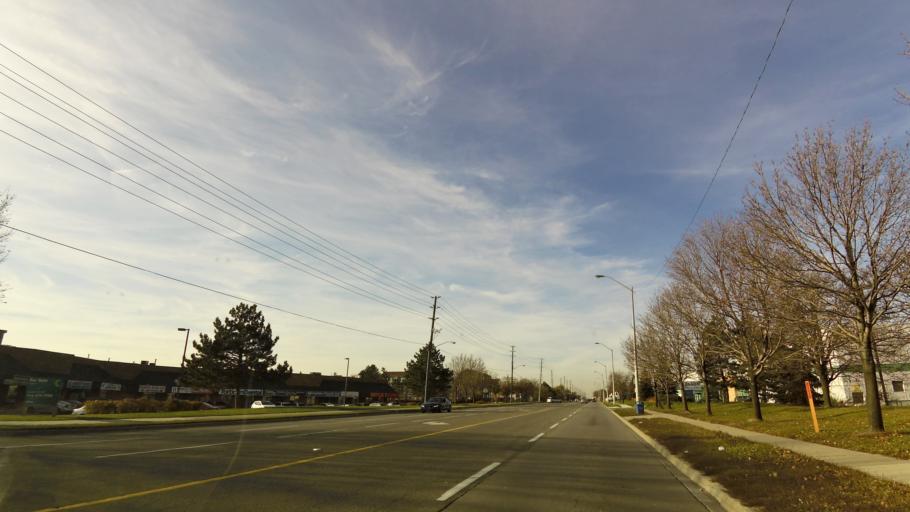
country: CA
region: Ontario
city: Brampton
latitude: 43.7249
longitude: -79.6941
